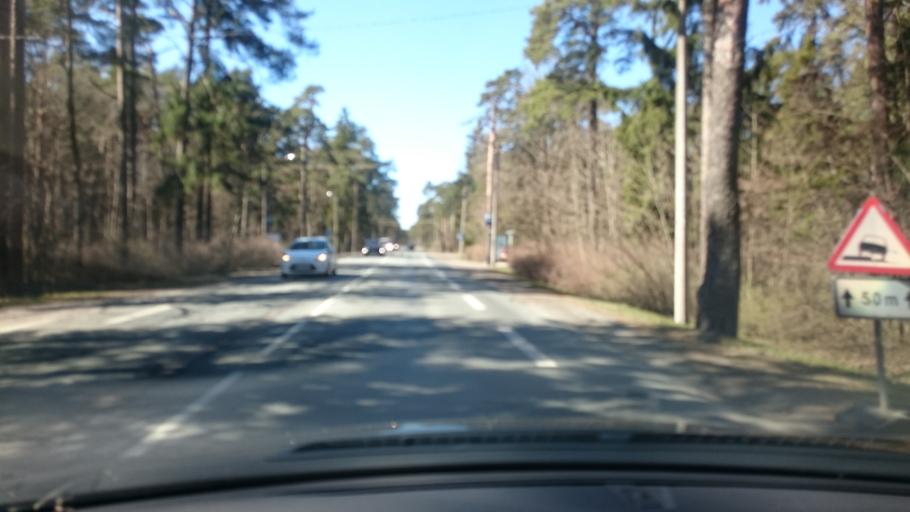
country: EE
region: Harju
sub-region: Tallinna linn
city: Kose
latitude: 59.4591
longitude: 24.8472
